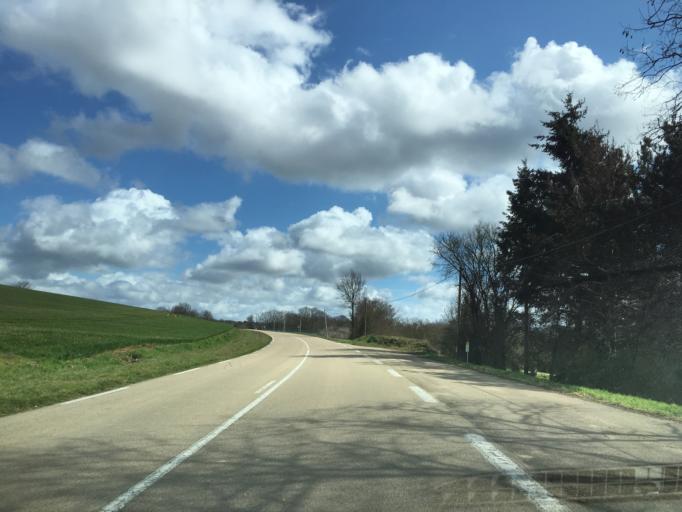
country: FR
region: Bourgogne
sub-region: Departement de l'Yonne
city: Charbuy
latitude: 47.8240
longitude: 3.4256
